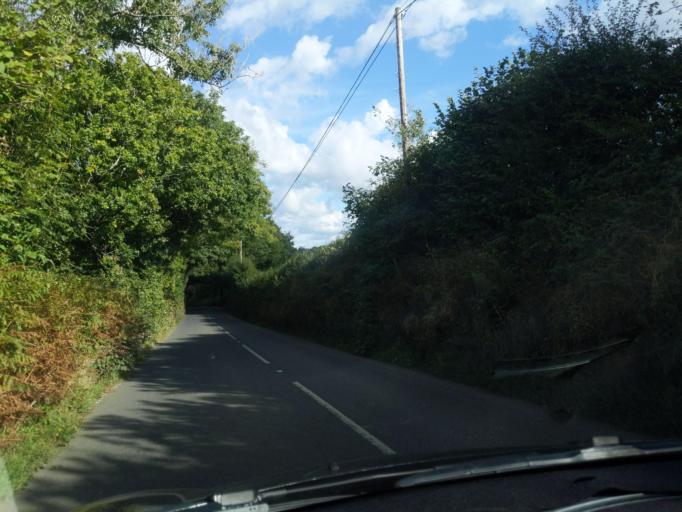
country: GB
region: England
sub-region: Devon
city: Great Torrington
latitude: 50.9439
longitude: -4.1641
